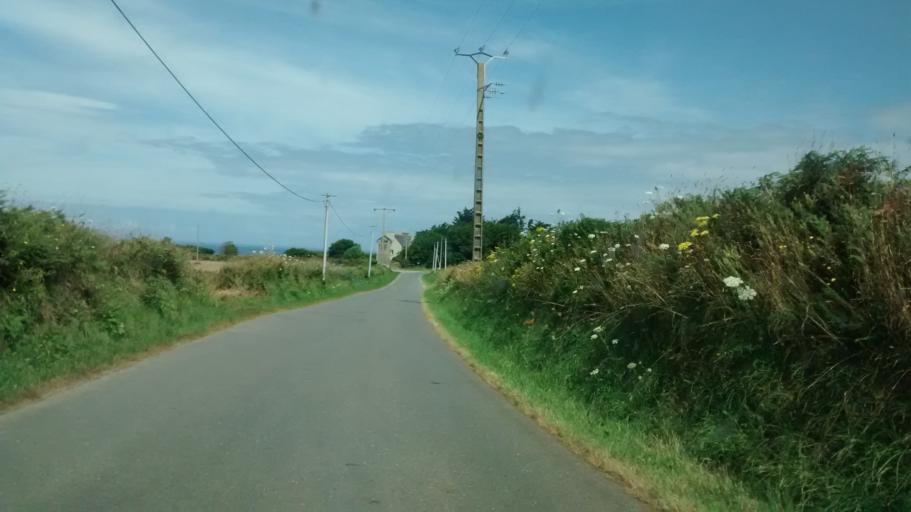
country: FR
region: Brittany
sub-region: Departement du Finistere
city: Plouguerneau
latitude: 48.6142
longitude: -4.4800
